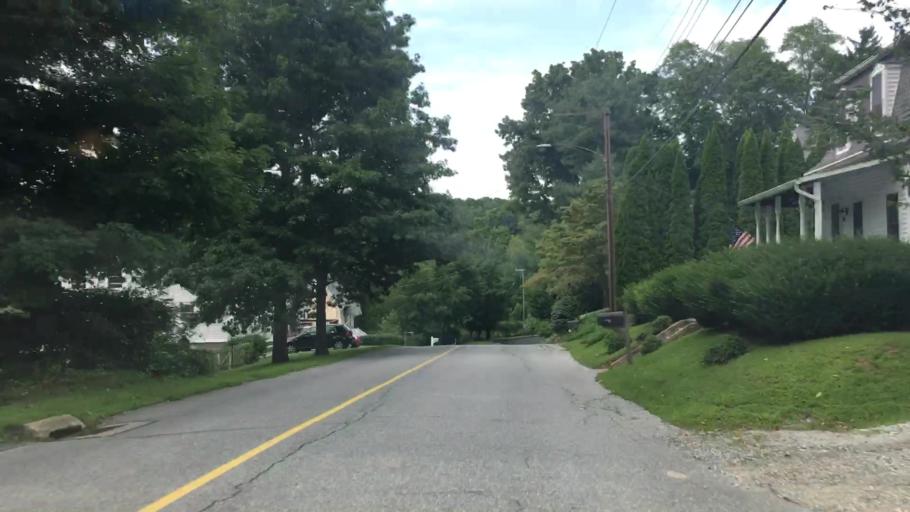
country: US
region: Connecticut
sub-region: Middlesex County
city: Deep River Center
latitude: 41.3443
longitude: -72.4464
